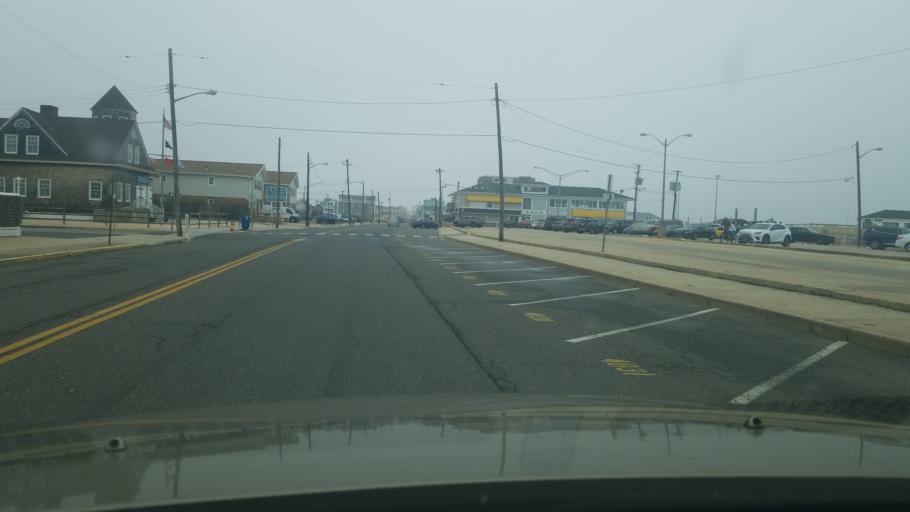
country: US
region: New Jersey
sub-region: Ocean County
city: Seaside Park
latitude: 39.9345
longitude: -74.0727
